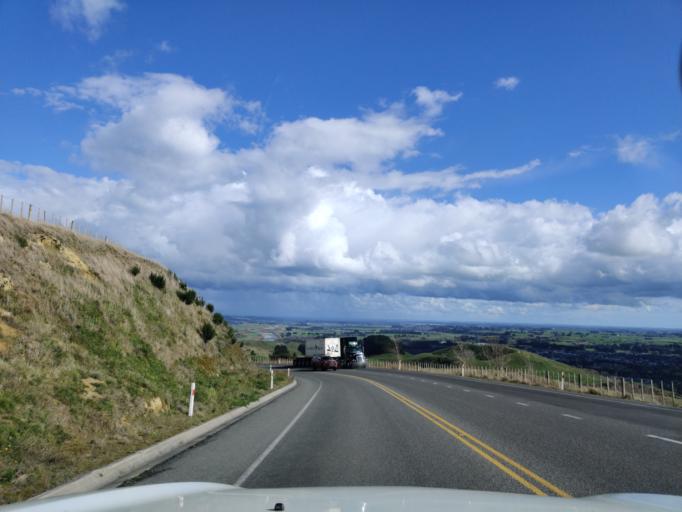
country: NZ
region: Manawatu-Wanganui
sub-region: Palmerston North City
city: Palmerston North
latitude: -40.2862
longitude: 175.7873
